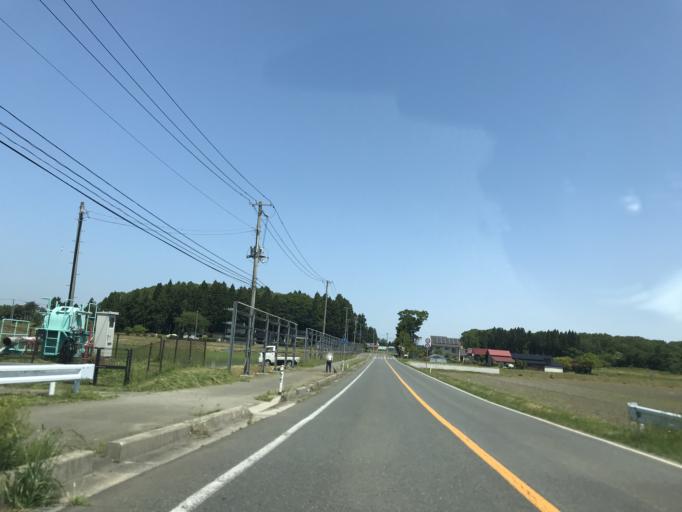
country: JP
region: Iwate
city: Kitakami
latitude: 39.2273
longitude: 141.0663
